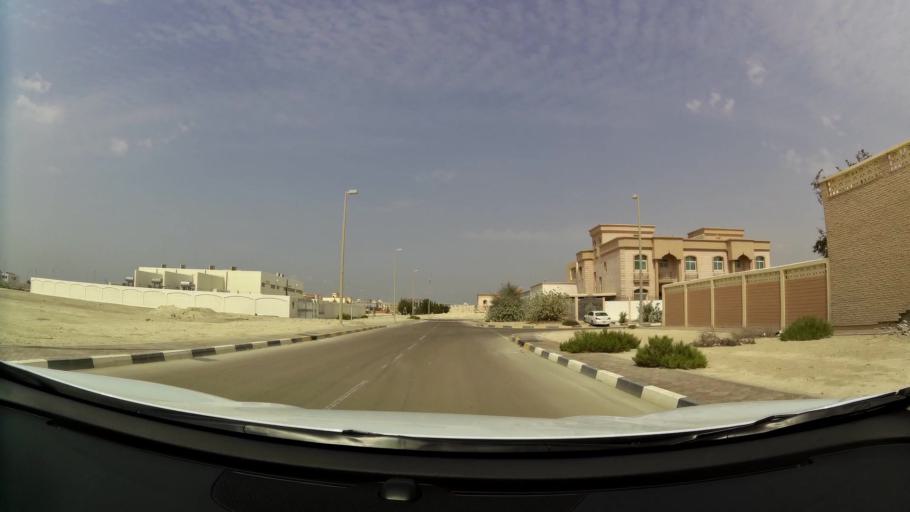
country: AE
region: Abu Dhabi
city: Abu Dhabi
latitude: 24.5261
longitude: 54.6826
